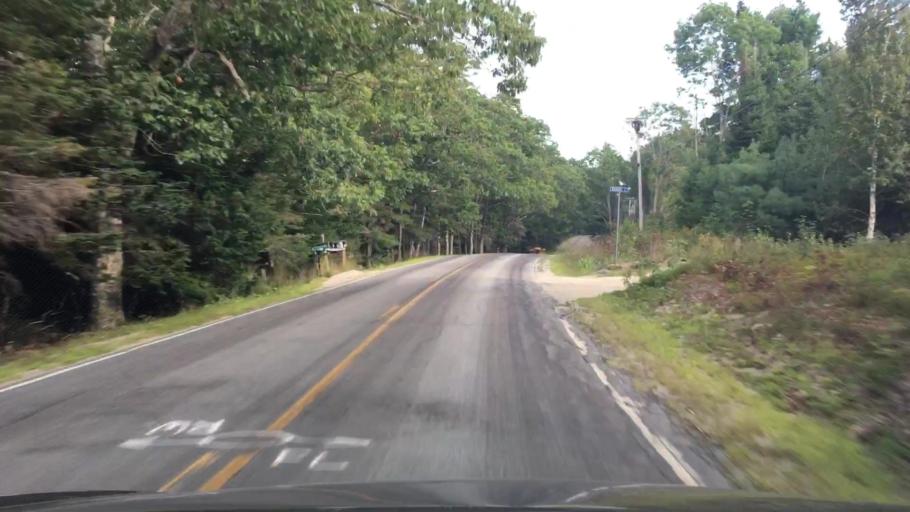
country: US
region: Maine
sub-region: Hancock County
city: Surry
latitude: 44.5121
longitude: -68.6000
